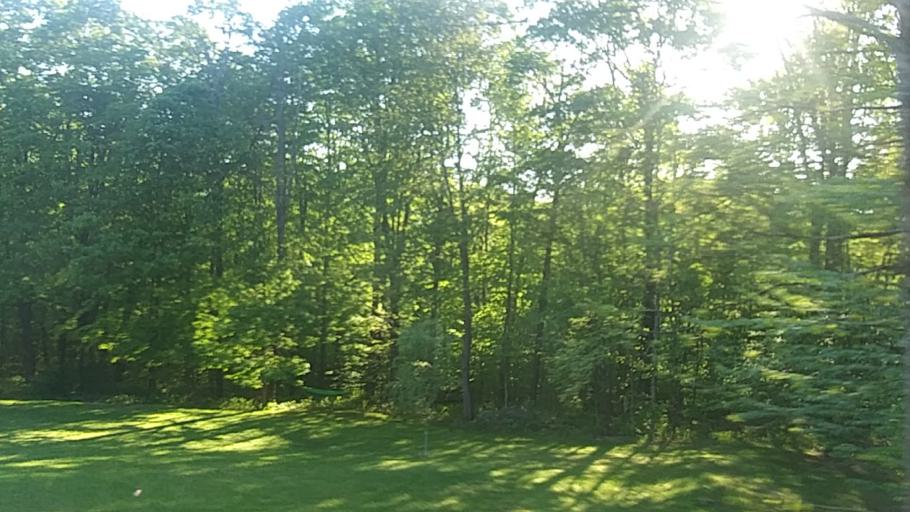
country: US
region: Massachusetts
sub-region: Franklin County
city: Shelburne Falls
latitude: 42.5917
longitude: -72.7459
